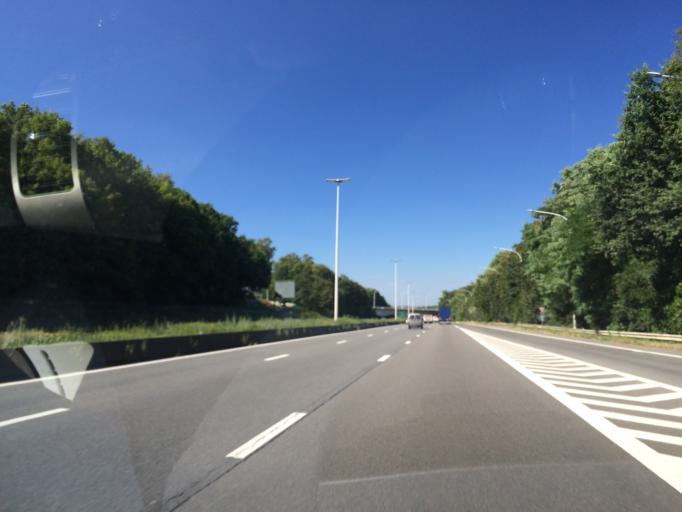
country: BE
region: Wallonia
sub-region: Province du Brabant Wallon
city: Wavre
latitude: 50.6972
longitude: 4.6183
